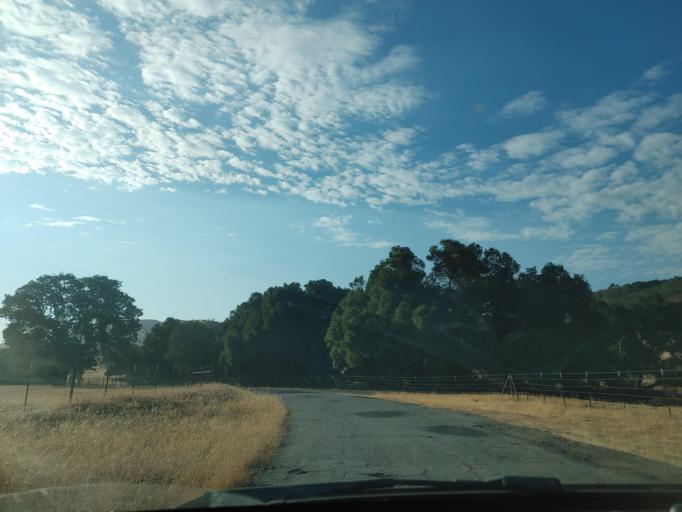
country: US
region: California
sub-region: San Benito County
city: Ridgemark
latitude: 36.7734
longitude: -121.2354
